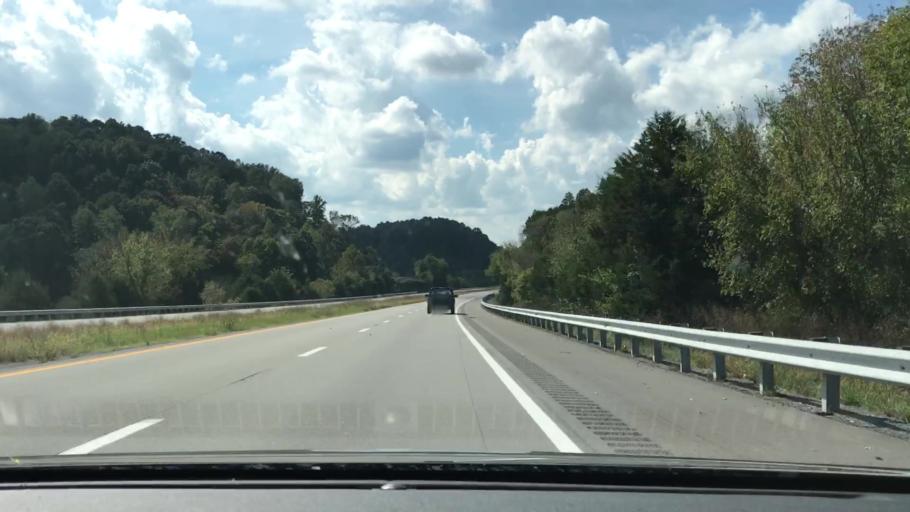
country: US
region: Kentucky
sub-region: Adair County
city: Columbia
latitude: 37.0584
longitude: -85.4264
